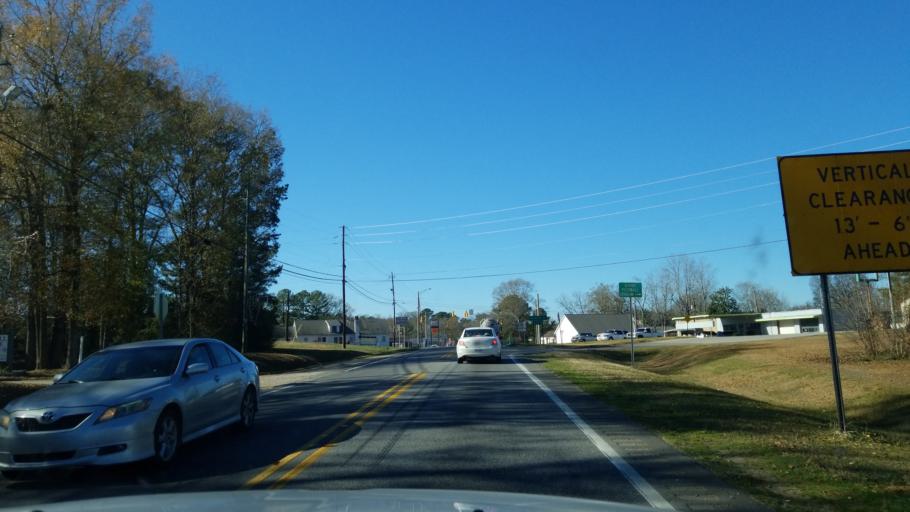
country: US
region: Alabama
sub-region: Pickens County
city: Gordo
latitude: 33.3159
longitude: -87.9016
